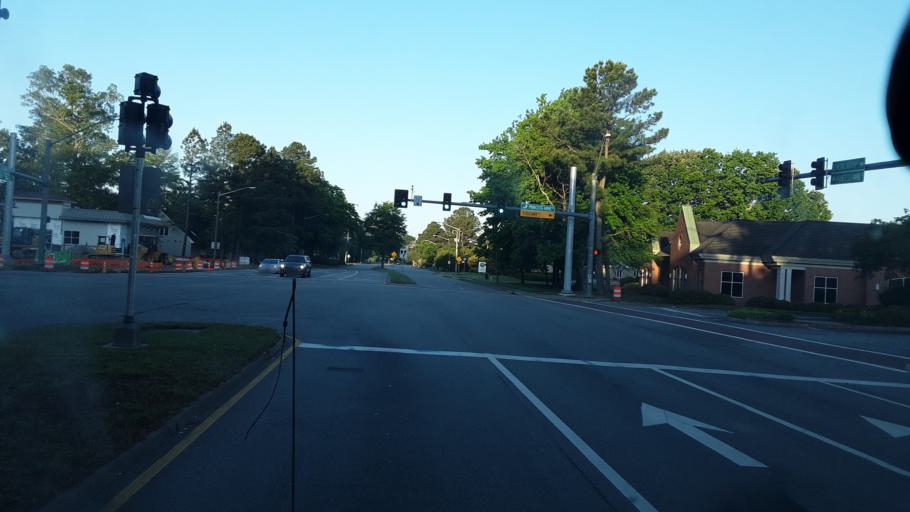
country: US
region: Virginia
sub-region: City of Virginia Beach
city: Virginia Beach
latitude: 36.7608
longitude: -76.0185
